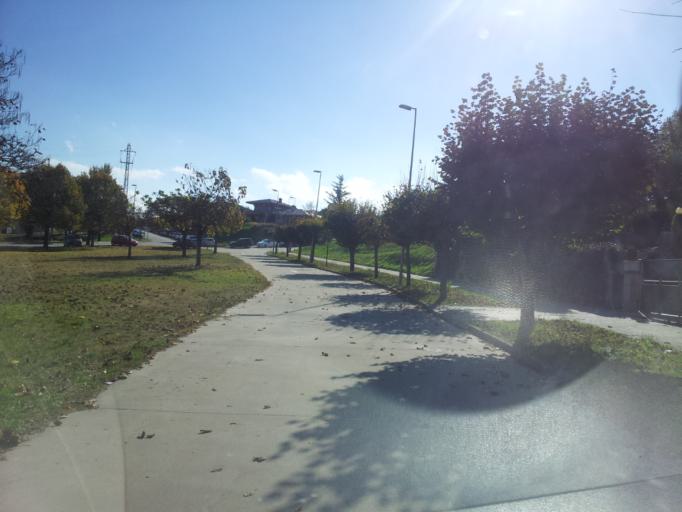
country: ES
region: Catalonia
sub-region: Provincia de Barcelona
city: Vic
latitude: 41.9351
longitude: 2.2377
